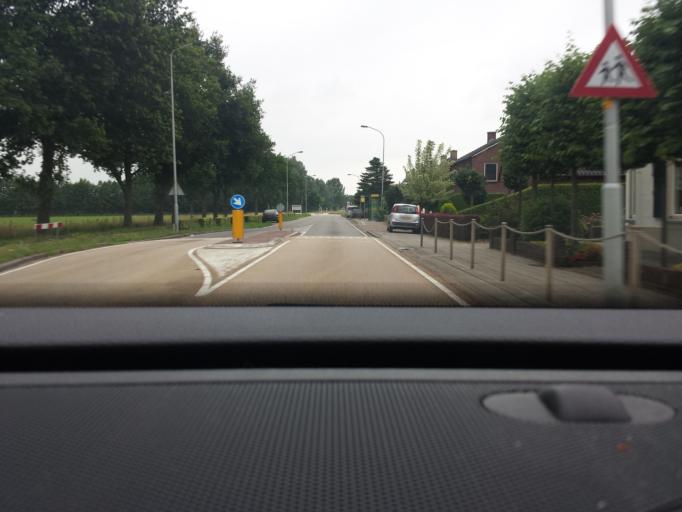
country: NL
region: Gelderland
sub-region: Gemeente Bronckhorst
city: Hengelo
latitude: 52.0110
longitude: 6.3042
